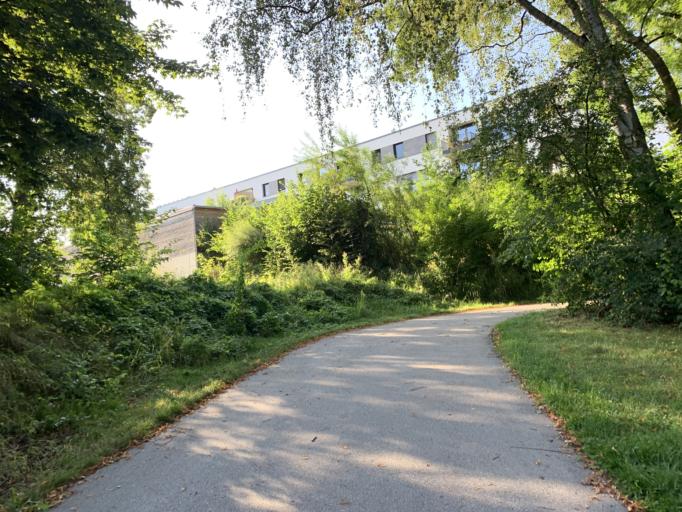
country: DE
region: Bavaria
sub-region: Upper Bavaria
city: Freising
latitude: 48.4096
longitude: 11.7522
